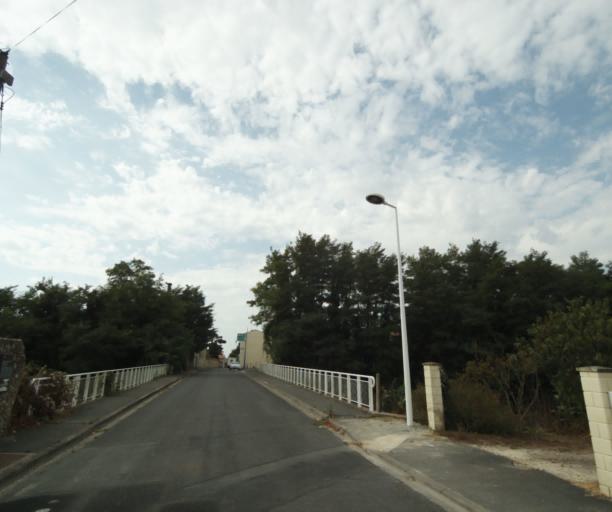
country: FR
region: Poitou-Charentes
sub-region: Departement de la Charente-Maritime
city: Tonnay-Charente
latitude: 45.9431
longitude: -0.8841
